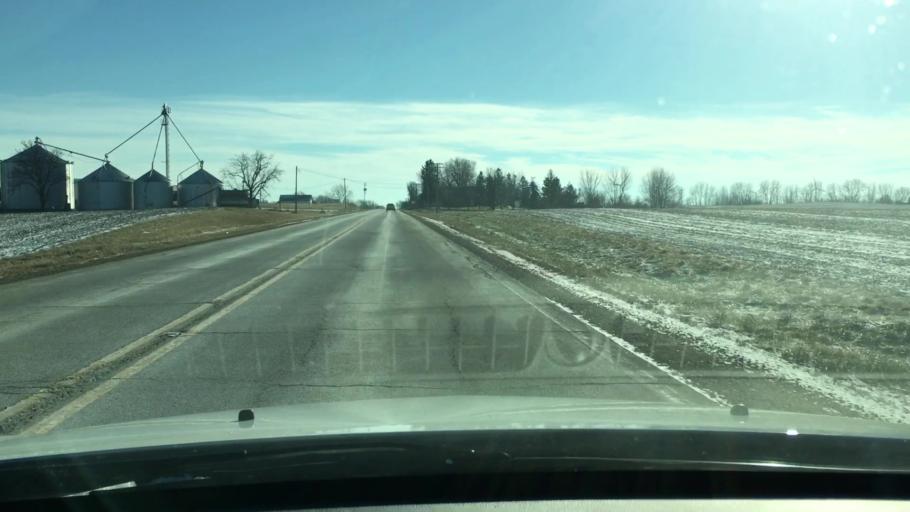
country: US
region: Illinois
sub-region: LaSalle County
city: Mendota
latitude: 41.7014
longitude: -89.0915
